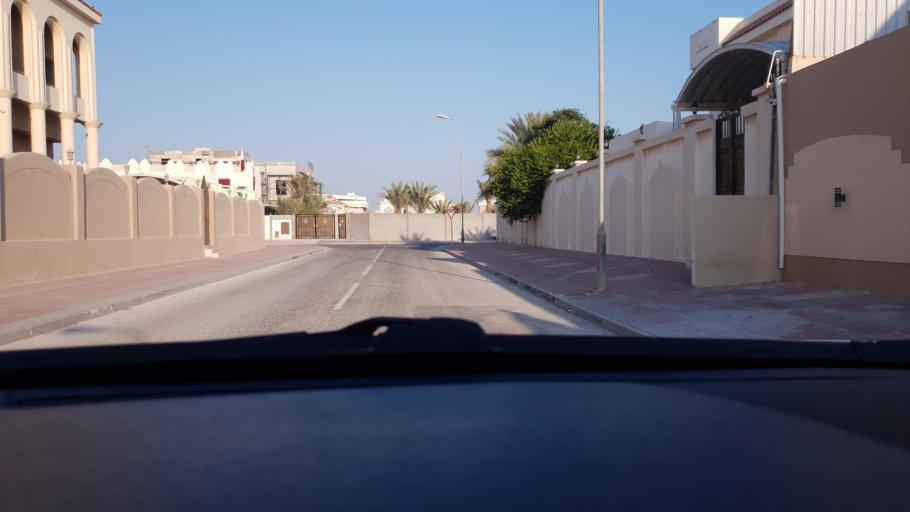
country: QA
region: Baladiyat ad Dawhah
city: Doha
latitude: 25.2352
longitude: 51.5596
